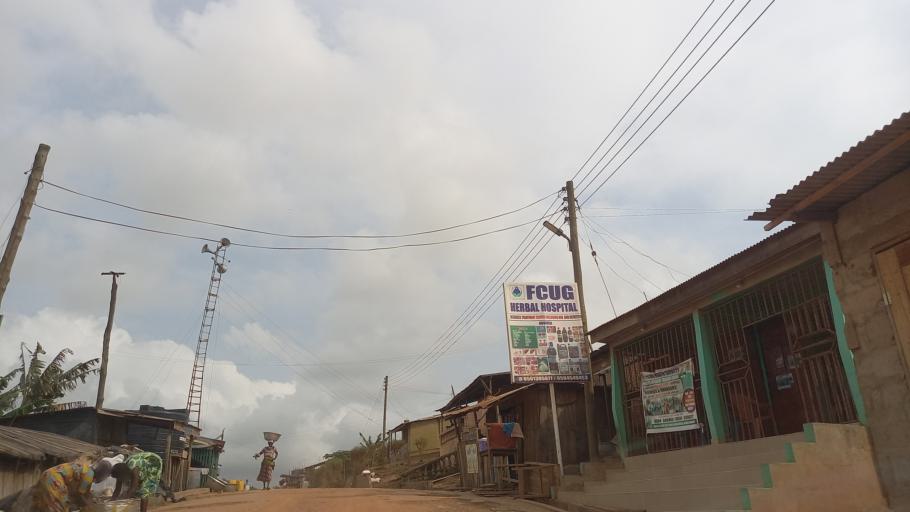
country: GH
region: Western
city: Shama Junction
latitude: 4.9843
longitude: -1.6376
